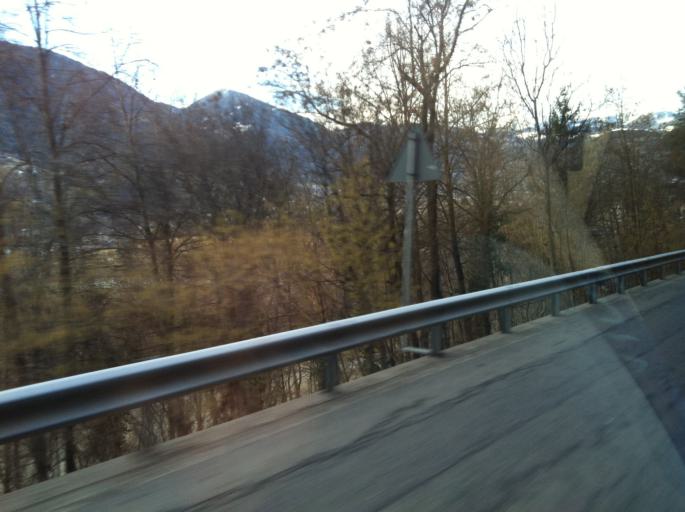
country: IT
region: Trentino-Alto Adige
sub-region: Bolzano
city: Bressanone
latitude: 46.6988
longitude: 11.6605
